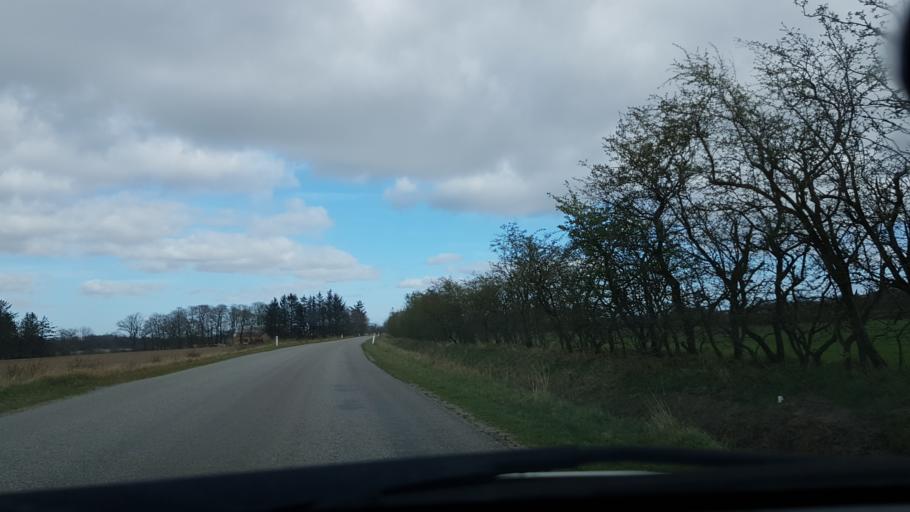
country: DK
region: South Denmark
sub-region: Vejen Kommune
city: Brorup
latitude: 55.4383
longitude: 9.0172
